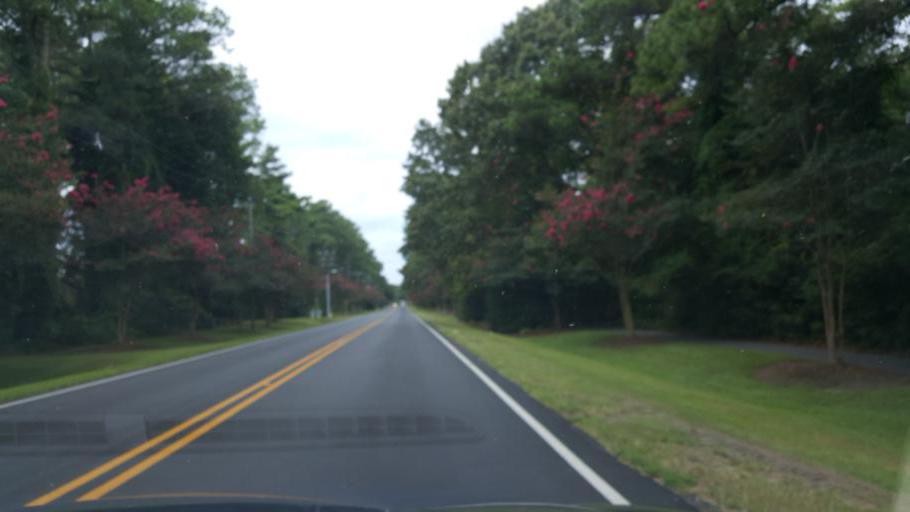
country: US
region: North Carolina
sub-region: Dare County
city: Manteo
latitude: 35.9331
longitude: -75.6954
